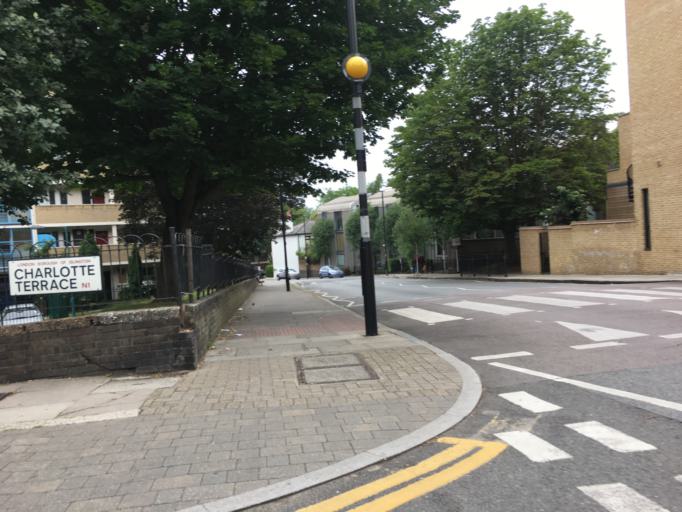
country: GB
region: England
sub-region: Greater London
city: Barnsbury
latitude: 51.5365
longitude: -0.1126
